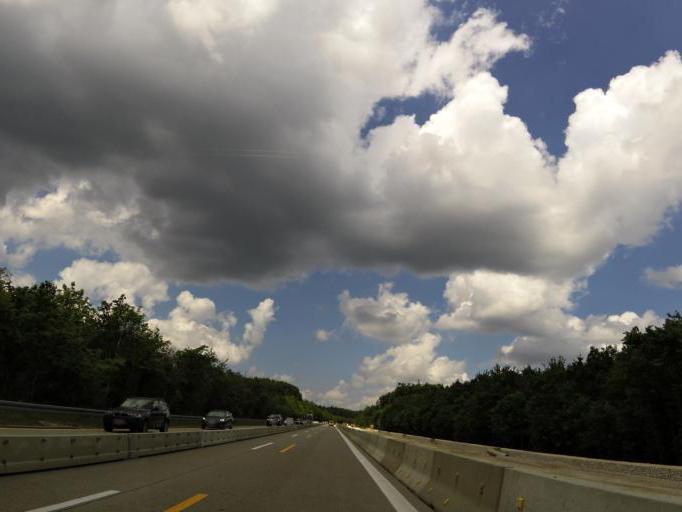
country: DE
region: Baden-Wuerttemberg
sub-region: Regierungsbezirk Stuttgart
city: Nattheim
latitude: 48.6736
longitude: 10.2221
